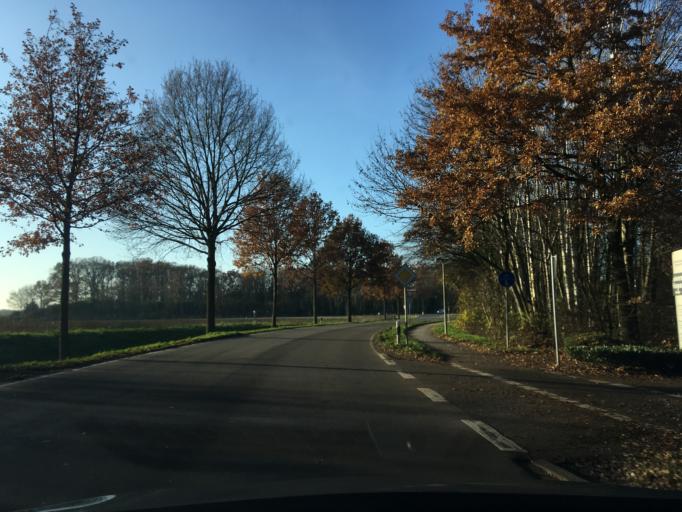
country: NL
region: Overijssel
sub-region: Gemeente Enschede
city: Enschede
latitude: 52.1263
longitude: 6.9085
